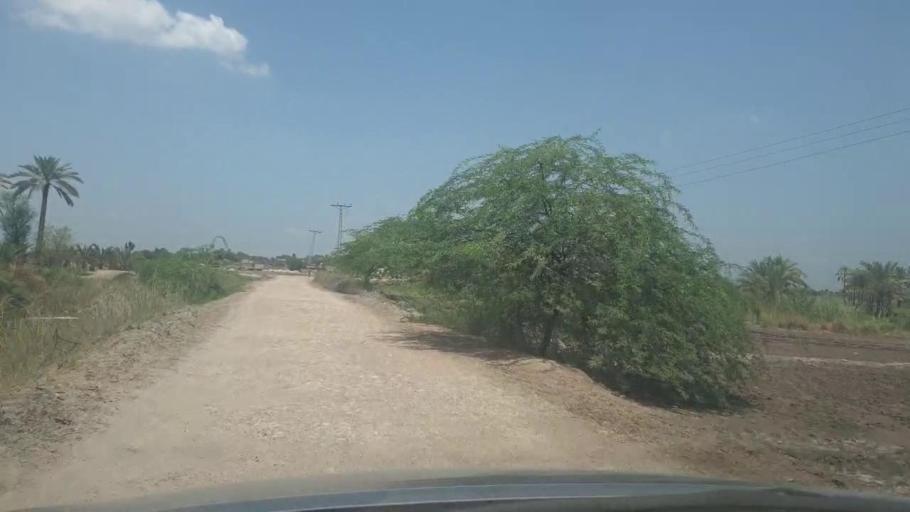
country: PK
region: Sindh
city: Kot Diji
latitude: 27.4168
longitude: 68.7362
